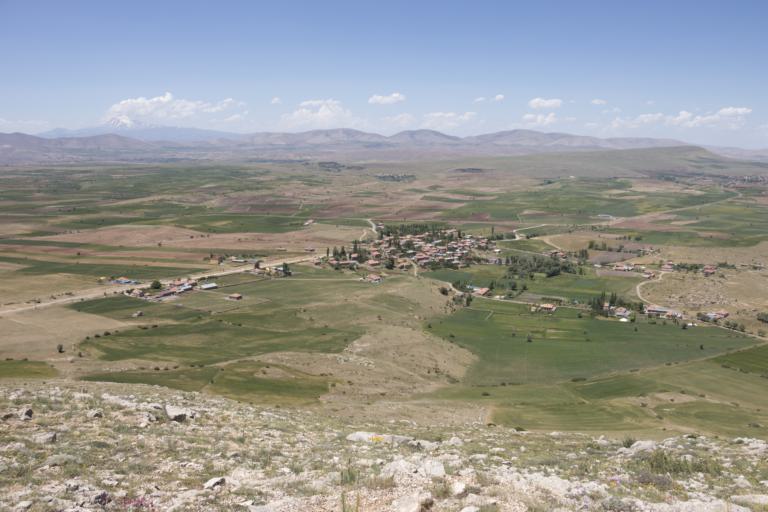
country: TR
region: Kayseri
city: Toklar
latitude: 38.4142
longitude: 36.1051
